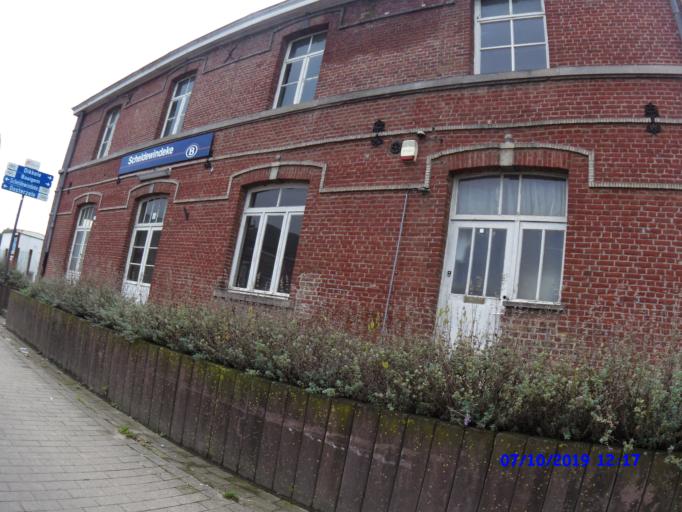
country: BE
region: Flanders
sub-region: Provincie Oost-Vlaanderen
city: Oosterzele
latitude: 50.9371
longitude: 3.7782
